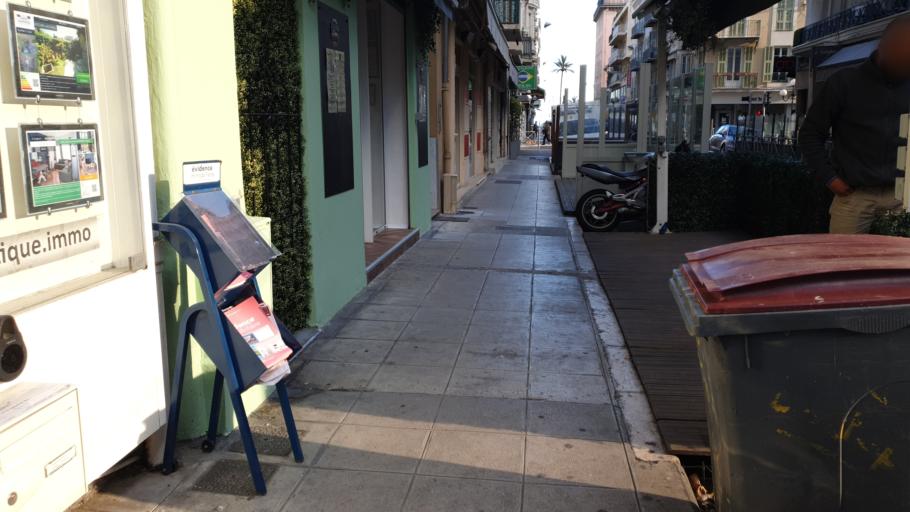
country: FR
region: Provence-Alpes-Cote d'Azur
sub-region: Departement des Alpes-Maritimes
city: Nice
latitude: 43.6963
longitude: 7.2607
